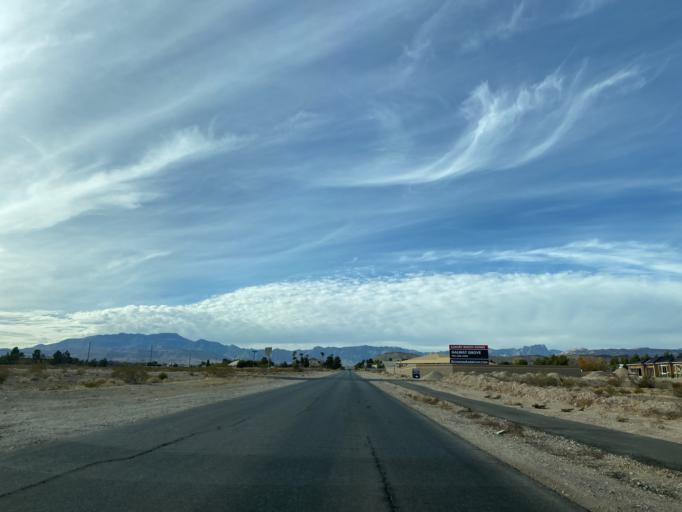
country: US
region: Nevada
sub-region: Clark County
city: Enterprise
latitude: 36.0337
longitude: -115.2689
